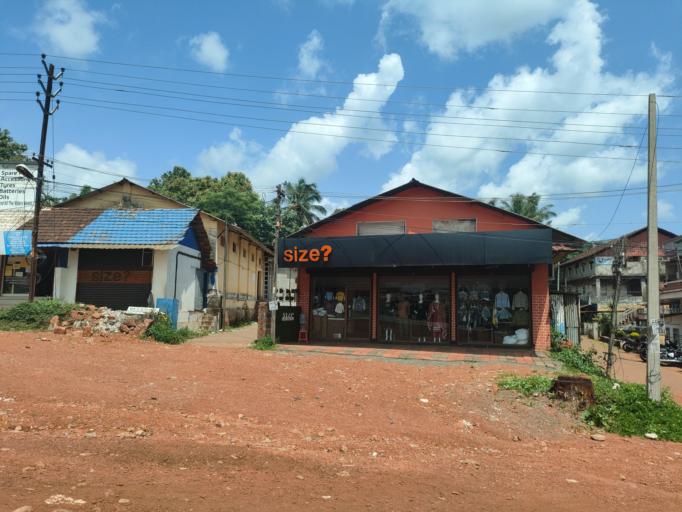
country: IN
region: Kerala
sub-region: Kasaragod District
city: Kasaragod
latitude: 12.5163
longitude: 75.0100
